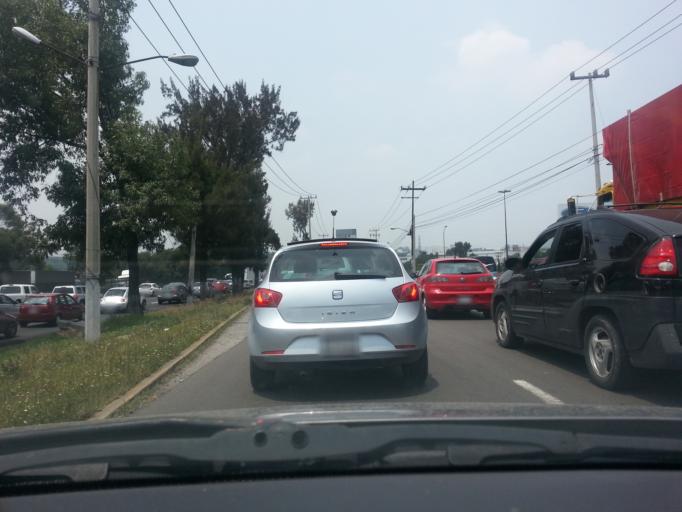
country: MX
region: Mexico
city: Cuautitlan Izcalli
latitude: 19.6465
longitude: -99.1959
